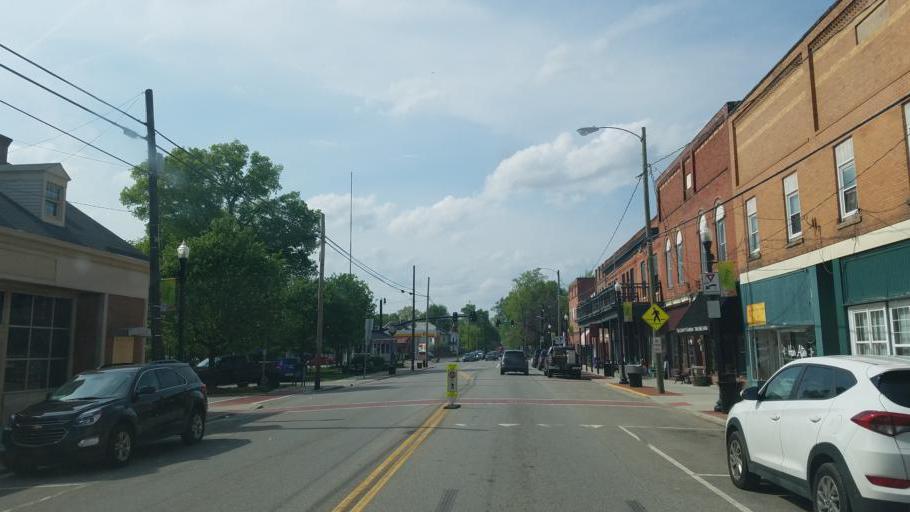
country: US
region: Ohio
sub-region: Licking County
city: Johnstown
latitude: 40.1531
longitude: -82.6841
